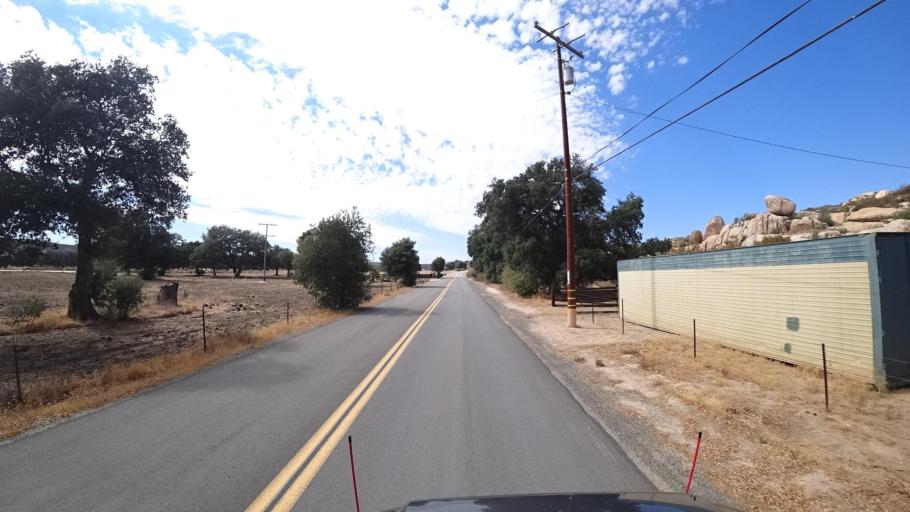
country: MX
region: Baja California
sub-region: Tecate
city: Cereso del Hongo
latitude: 32.6424
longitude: -116.2769
